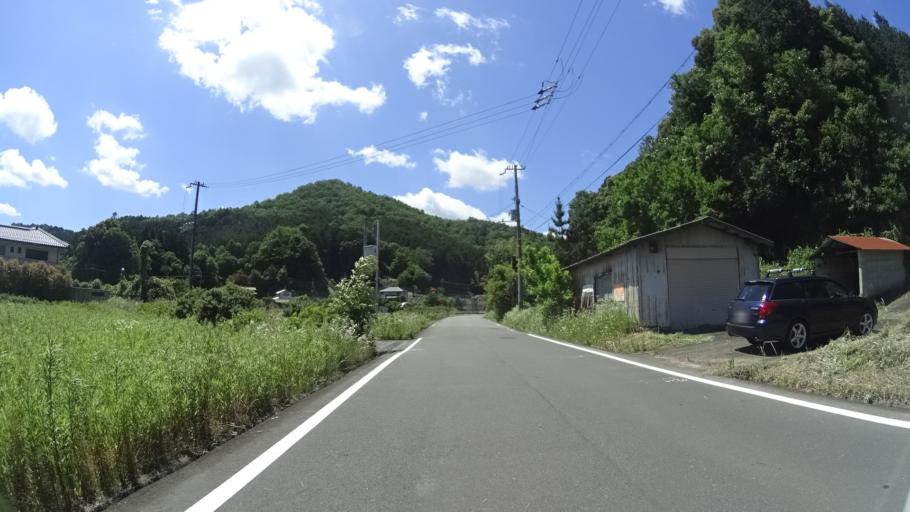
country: JP
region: Kyoto
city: Miyazu
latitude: 35.4110
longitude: 135.1906
